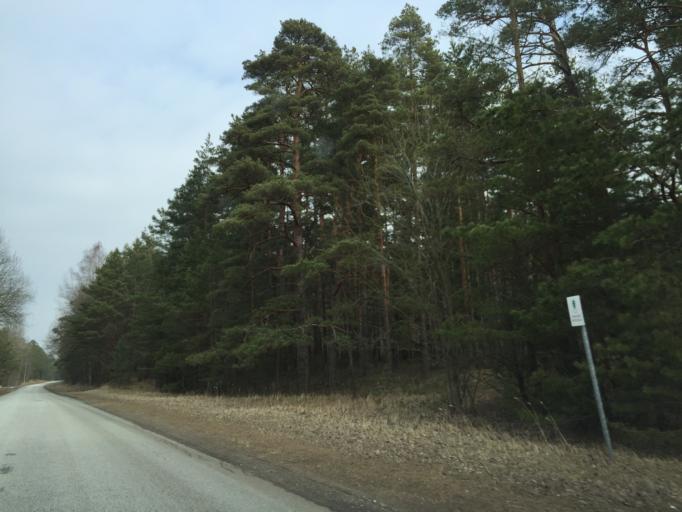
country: LV
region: Salacgrivas
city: Ainazi
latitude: 57.9560
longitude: 24.3990
